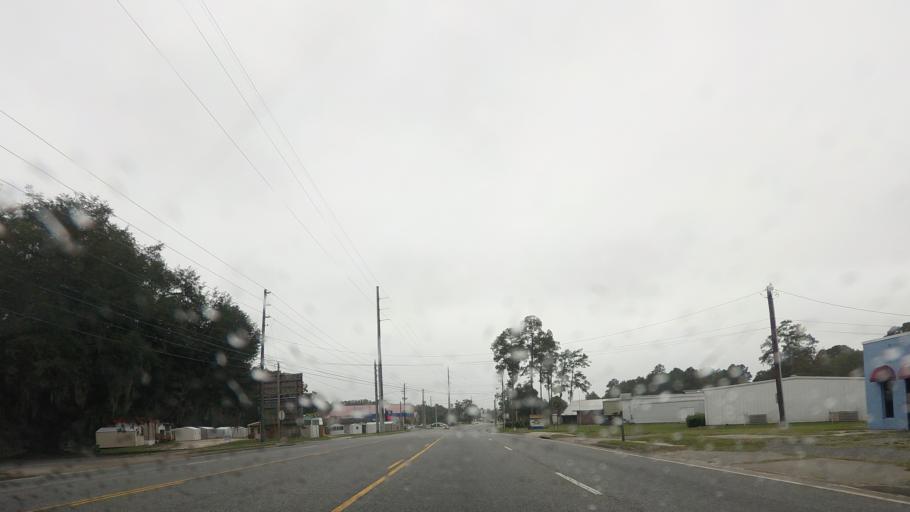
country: US
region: Georgia
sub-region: Lowndes County
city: Remerton
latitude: 30.8308
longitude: -83.3100
